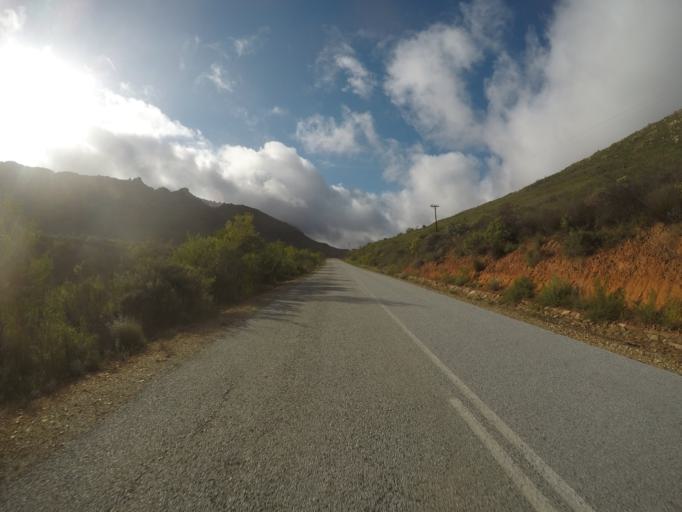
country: ZA
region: Western Cape
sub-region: West Coast District Municipality
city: Clanwilliam
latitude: -32.3666
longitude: 18.8608
